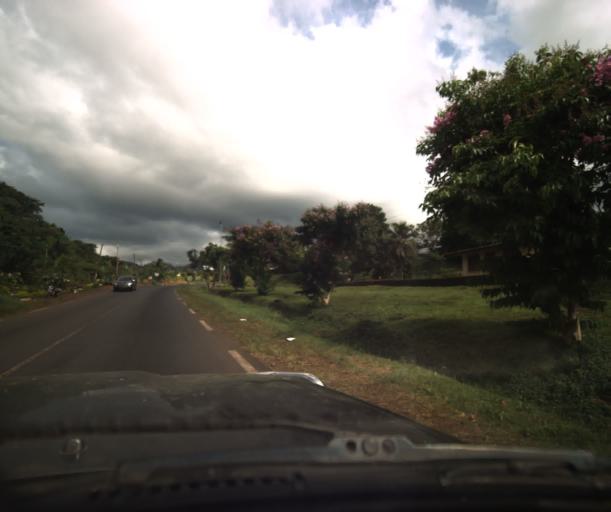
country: CM
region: South-West Province
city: Limbe
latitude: 4.0184
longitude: 9.1842
